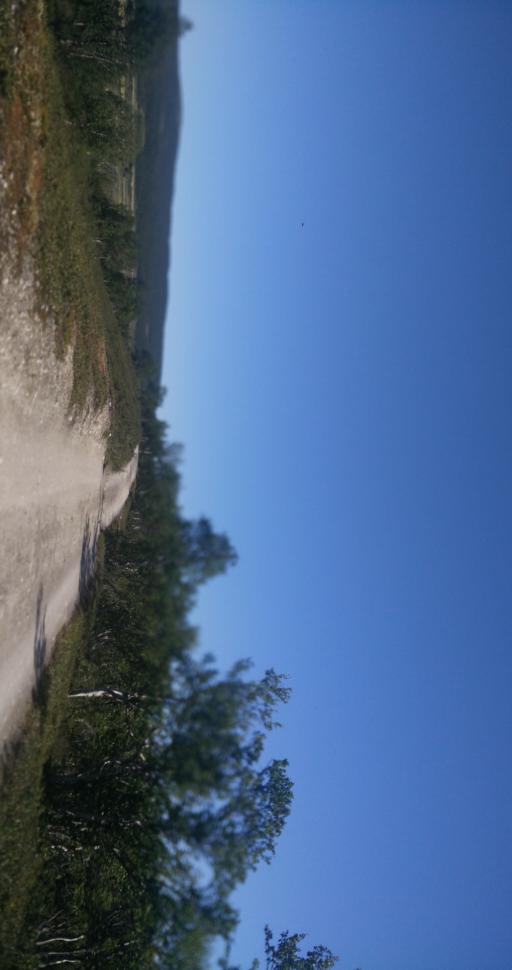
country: SE
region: Jaemtland
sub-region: Are Kommun
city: Are
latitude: 62.7081
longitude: 12.5037
